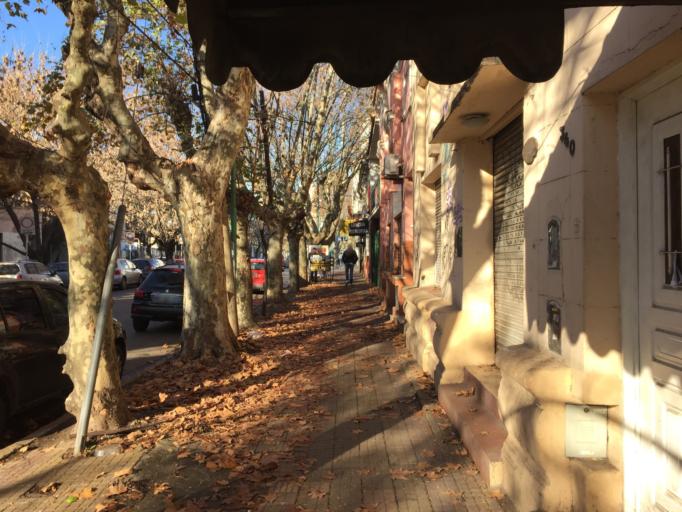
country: AR
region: Buenos Aires
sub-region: Partido de Lomas de Zamora
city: Lomas de Zamora
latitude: -34.7560
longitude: -58.4032
